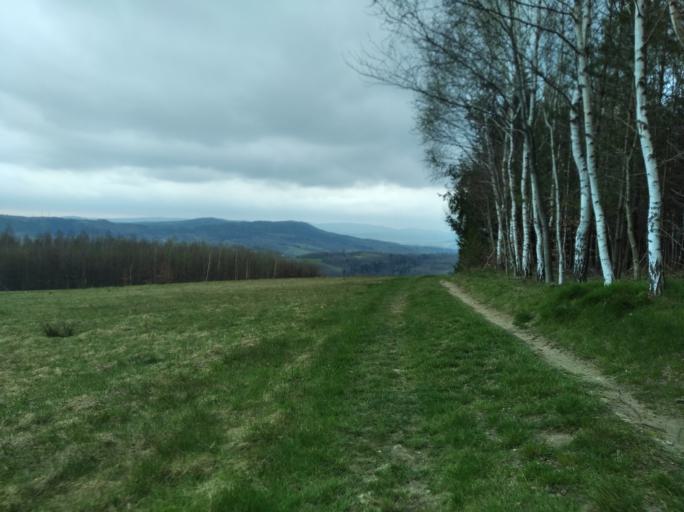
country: PL
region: Subcarpathian Voivodeship
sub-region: Powiat strzyzowski
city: Konieczkowa
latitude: 49.8176
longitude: 21.9355
